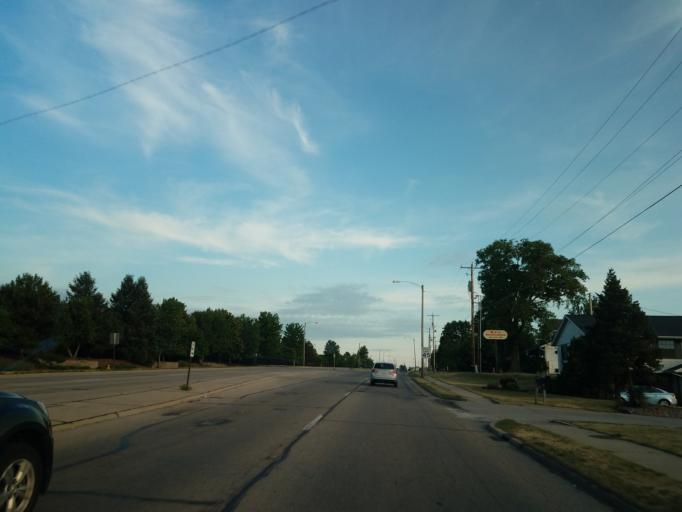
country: US
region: Illinois
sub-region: McLean County
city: Bloomington
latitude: 40.4560
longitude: -88.9928
